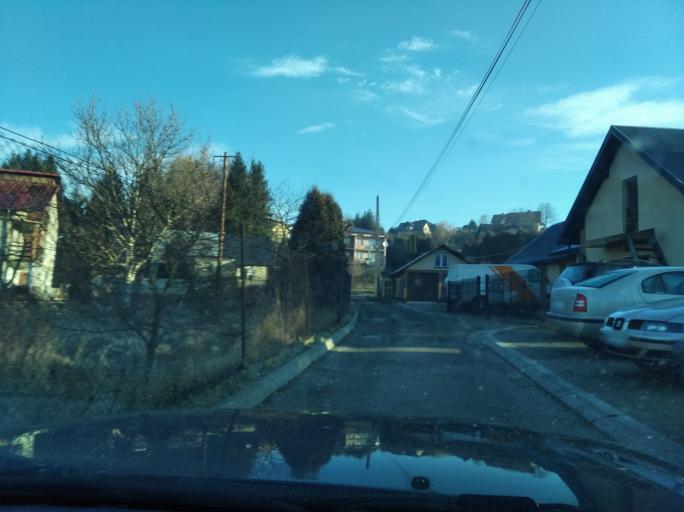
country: PL
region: Subcarpathian Voivodeship
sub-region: Powiat strzyzowski
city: Strzyzow
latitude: 49.8708
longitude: 21.8043
